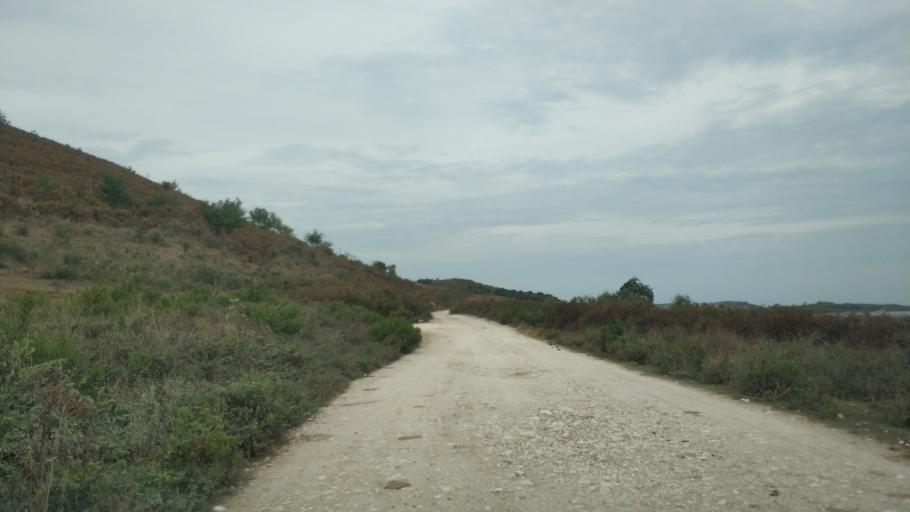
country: AL
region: Vlore
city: Vlore
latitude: 40.5126
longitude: 19.3990
